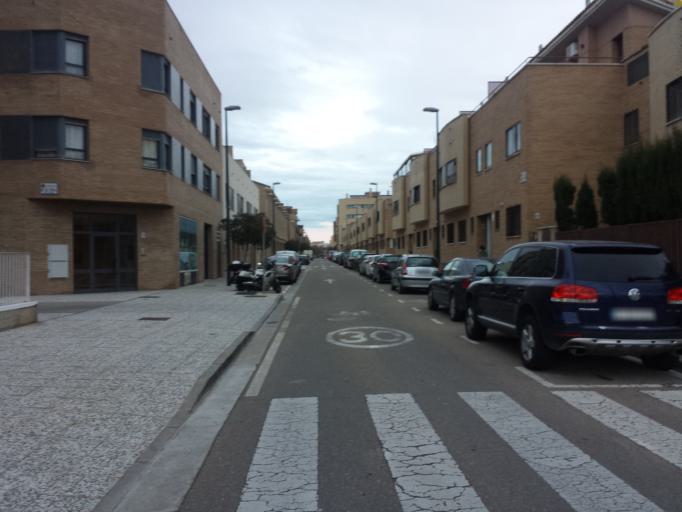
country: ES
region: Aragon
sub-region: Provincia de Zaragoza
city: Zaragoza
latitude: 41.6701
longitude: -0.8358
